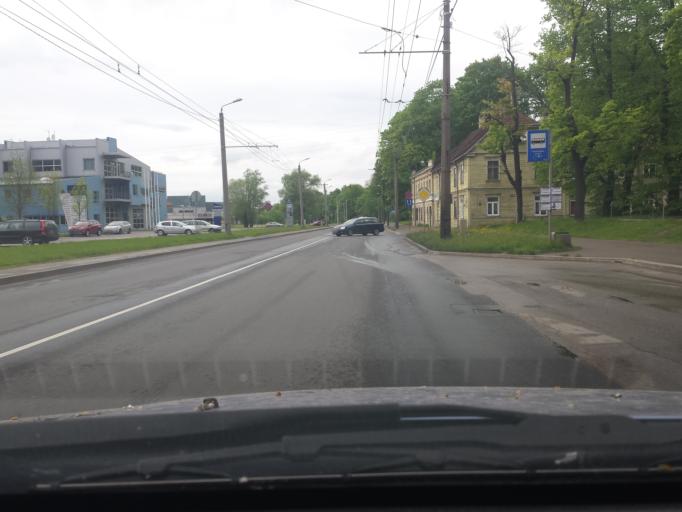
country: LV
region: Riga
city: Riga
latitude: 56.9836
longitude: 24.1361
